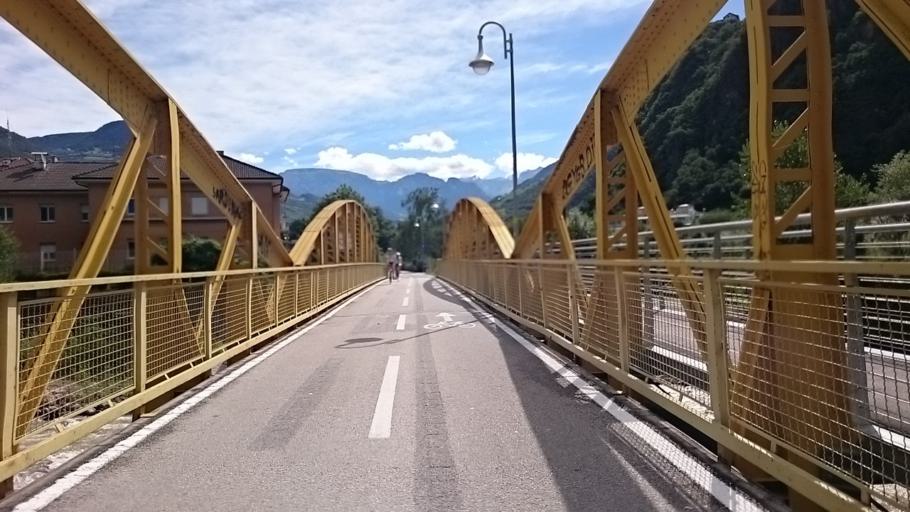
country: IT
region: Trentino-Alto Adige
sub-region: Bolzano
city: Bolzano
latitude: 46.4939
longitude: 11.3481
